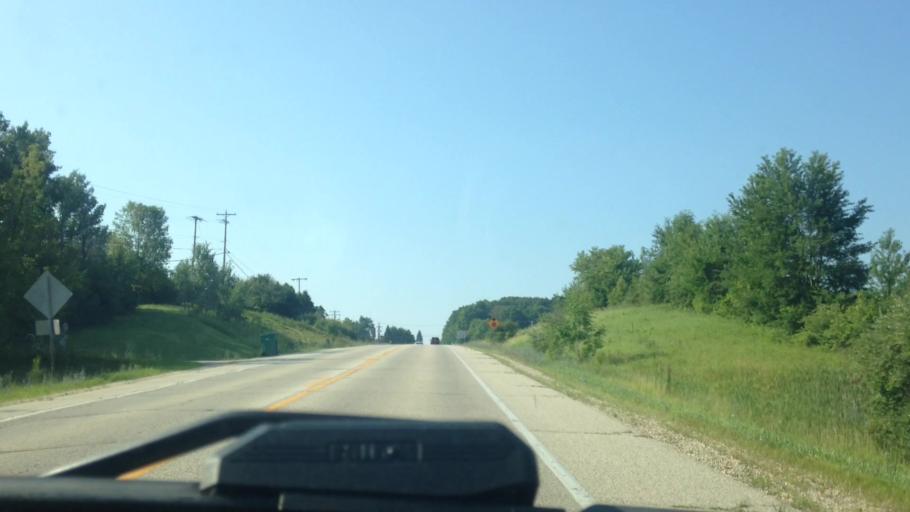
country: US
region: Wisconsin
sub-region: Washington County
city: Richfield
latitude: 43.2549
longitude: -88.2618
